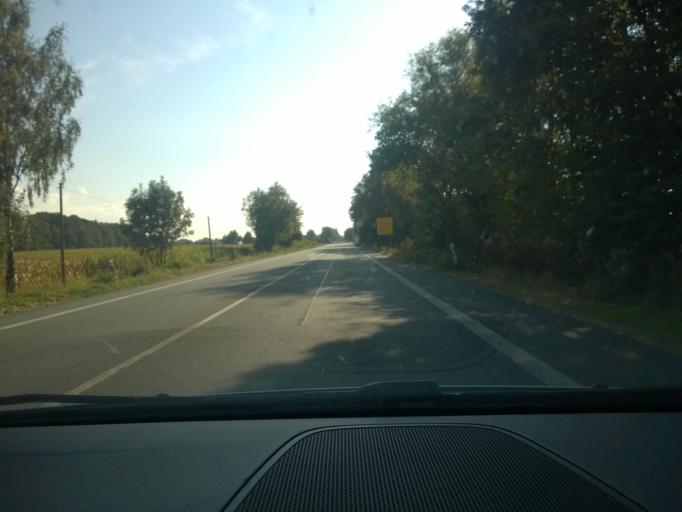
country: DE
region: North Rhine-Westphalia
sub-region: Regierungsbezirk Munster
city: Sudlohn
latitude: 51.9347
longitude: 6.8560
